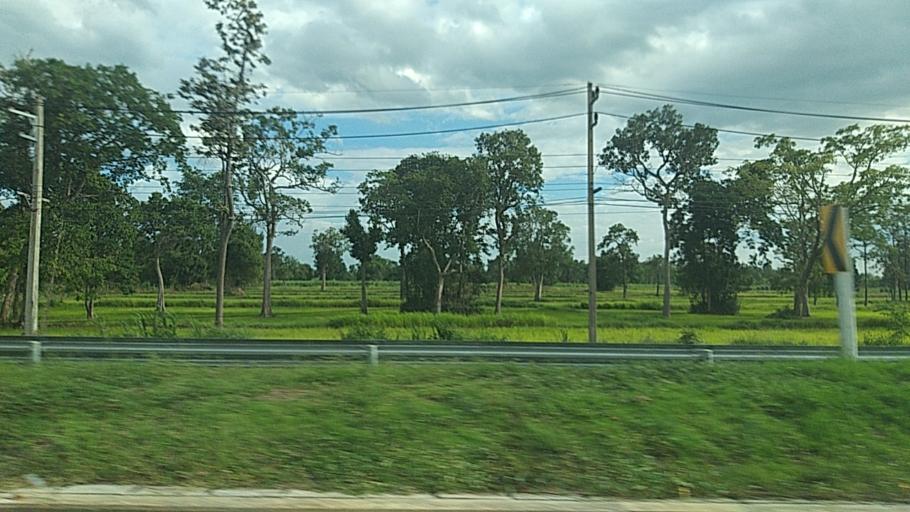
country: TH
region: Surin
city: Prasat
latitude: 14.5892
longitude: 103.4672
